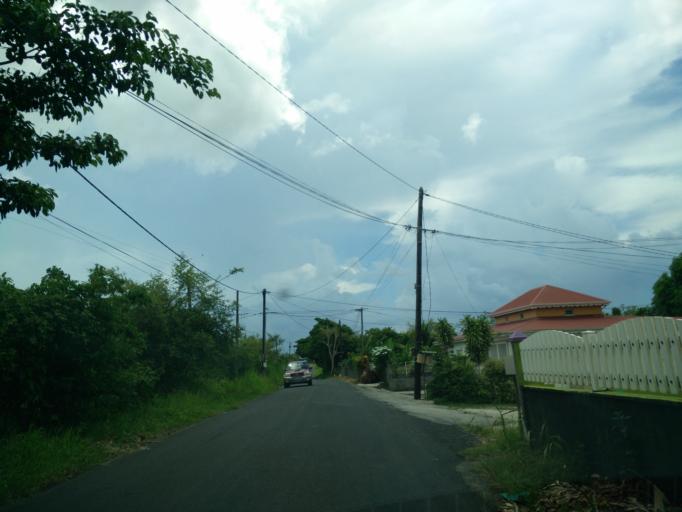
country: GP
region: Guadeloupe
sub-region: Guadeloupe
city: Saint-Francois
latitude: 16.2707
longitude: -61.3310
